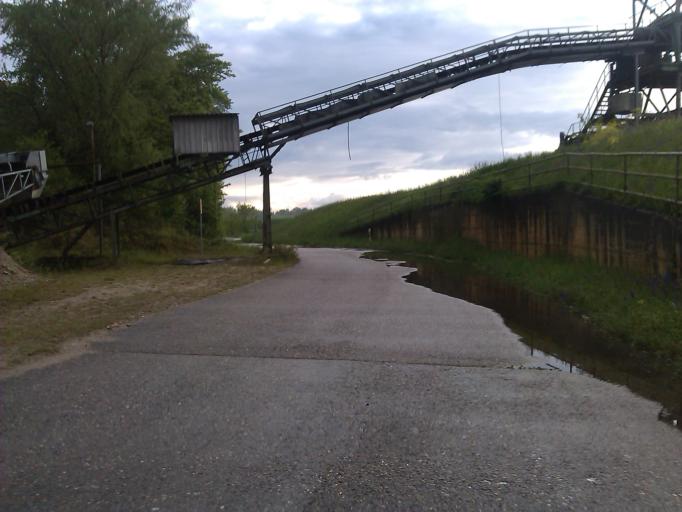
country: FR
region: Alsace
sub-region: Departement du Bas-Rhin
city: Drusenheim
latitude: 48.7429
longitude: 7.9706
